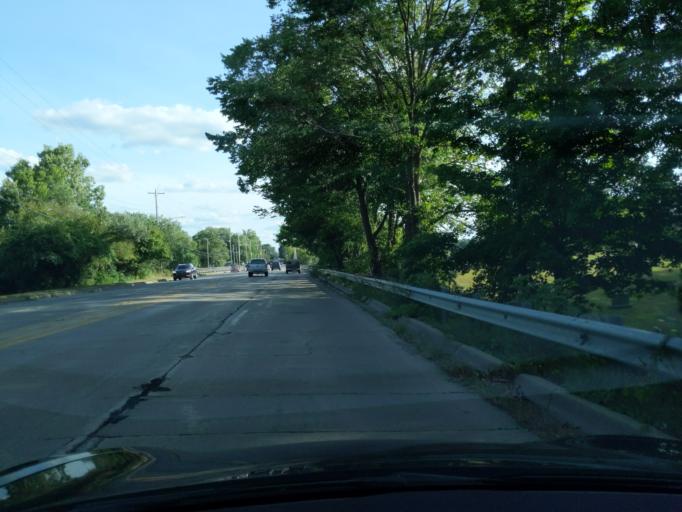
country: US
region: Michigan
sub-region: Eaton County
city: Waverly
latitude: 42.7105
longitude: -84.6031
